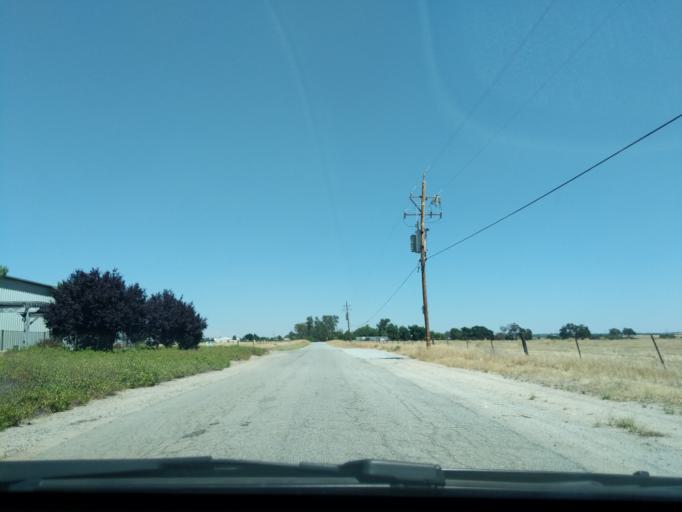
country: US
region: California
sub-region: San Luis Obispo County
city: Paso Robles
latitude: 35.6630
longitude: -120.6268
